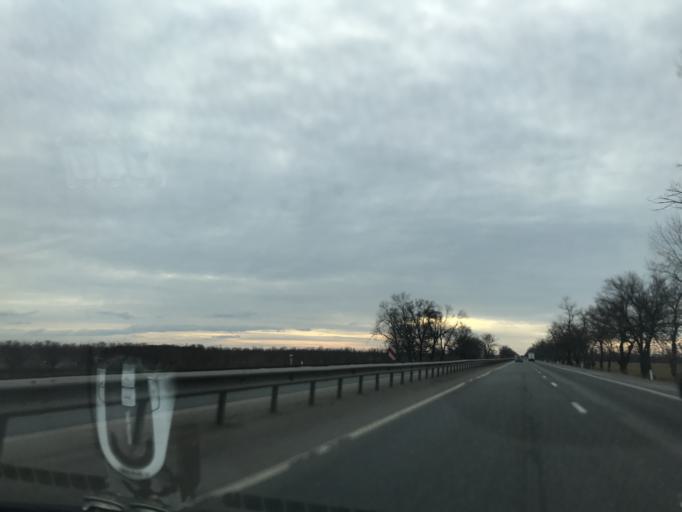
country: RU
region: Krasnodarskiy
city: Girey
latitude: 45.3408
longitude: 40.6052
